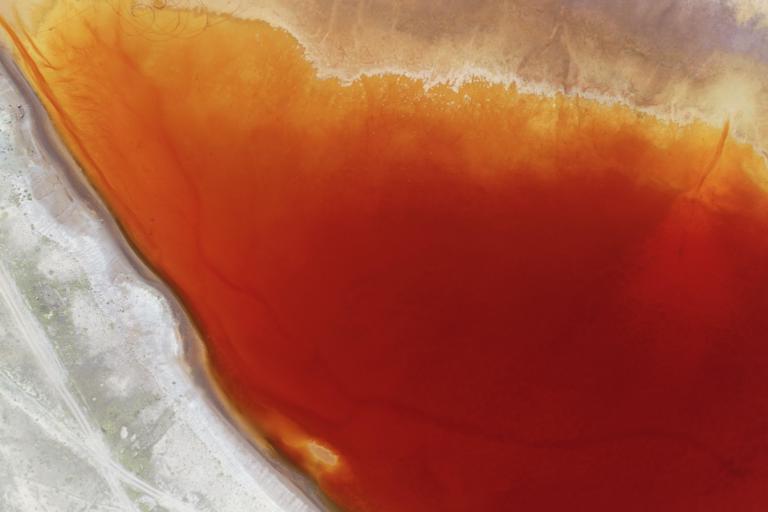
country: BO
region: La Paz
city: La Paz
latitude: -16.3425
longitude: -68.1624
